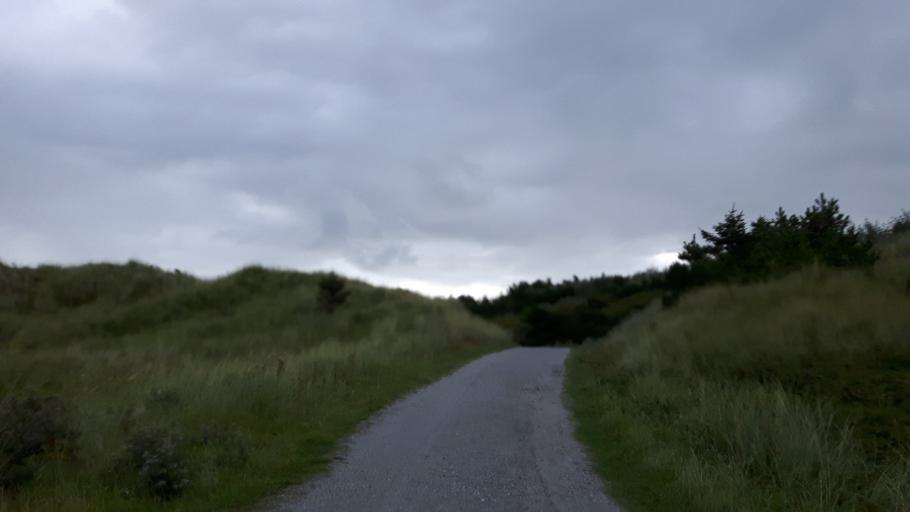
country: NL
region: Friesland
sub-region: Gemeente Ameland
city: Nes
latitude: 53.4573
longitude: 5.7604
